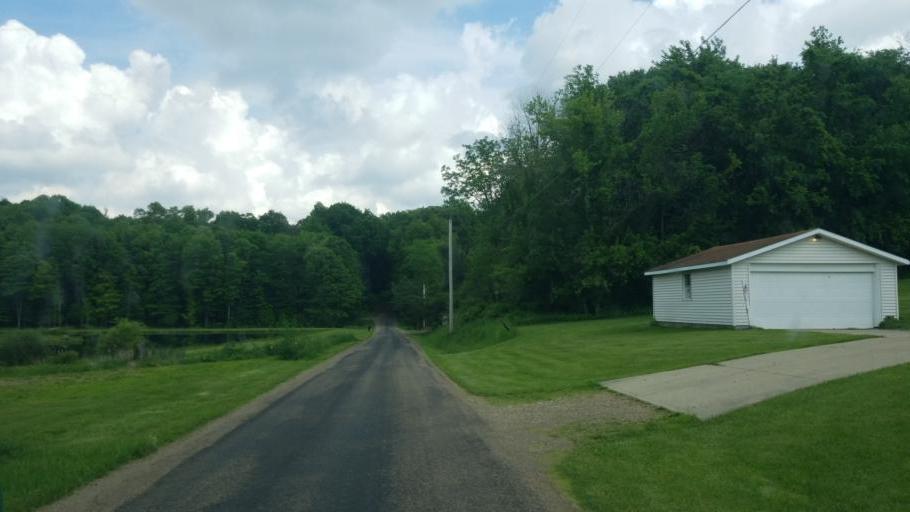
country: US
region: Ohio
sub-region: Sandusky County
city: Bellville
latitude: 40.6452
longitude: -82.4083
